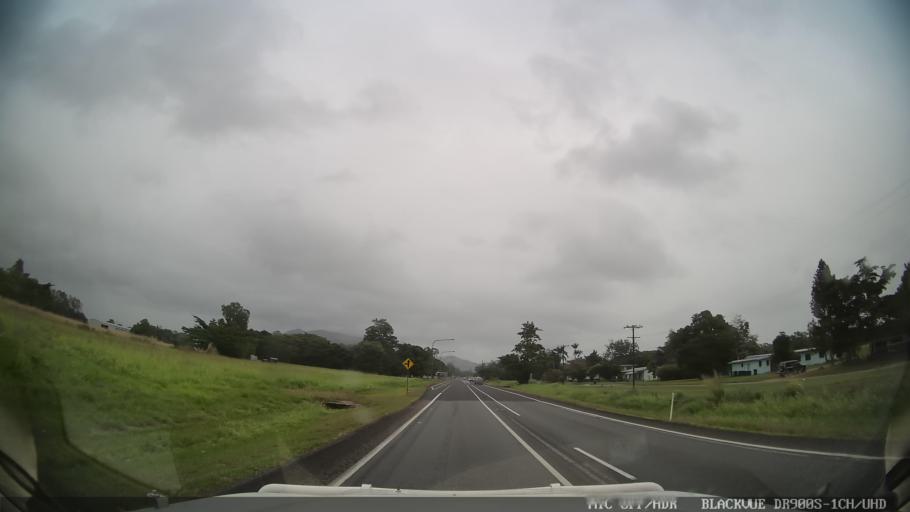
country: AU
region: Queensland
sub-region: Hinchinbrook
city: Ingham
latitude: -18.2068
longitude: 145.9585
